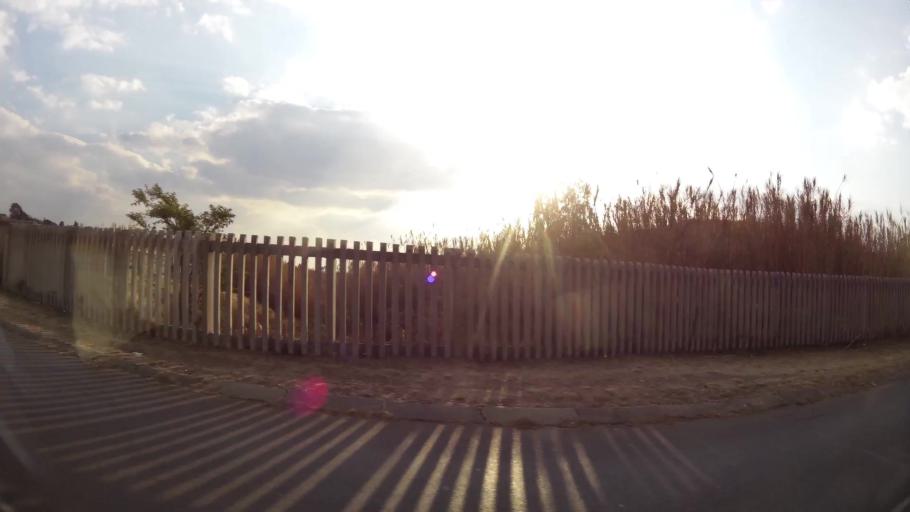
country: ZA
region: Gauteng
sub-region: City of Johannesburg Metropolitan Municipality
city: Modderfontein
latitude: -26.1311
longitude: 28.1840
